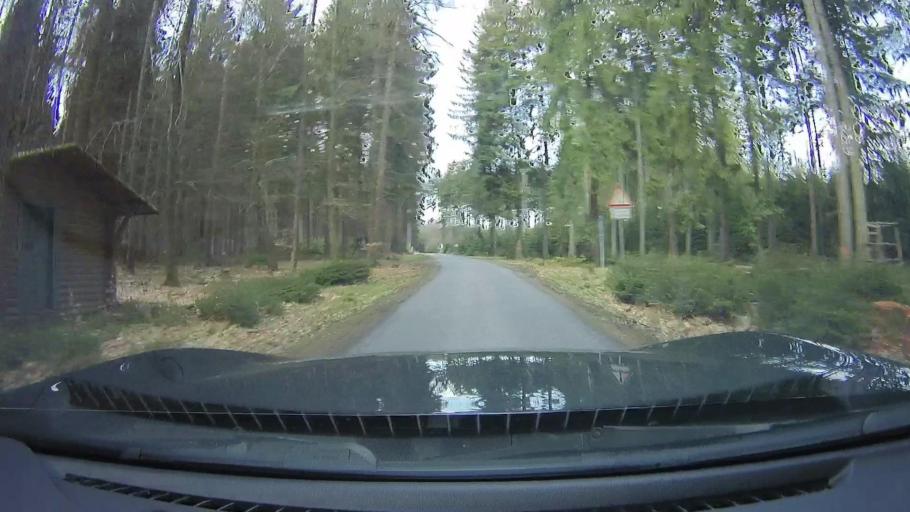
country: DE
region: Hesse
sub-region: Regierungsbezirk Darmstadt
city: Hesseneck
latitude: 49.6008
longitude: 9.0822
